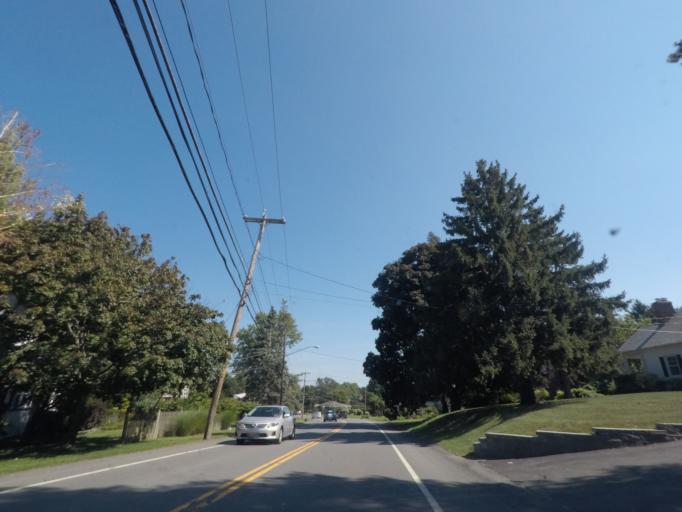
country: US
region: New York
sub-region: Albany County
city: Menands
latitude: 42.7349
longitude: -73.7568
